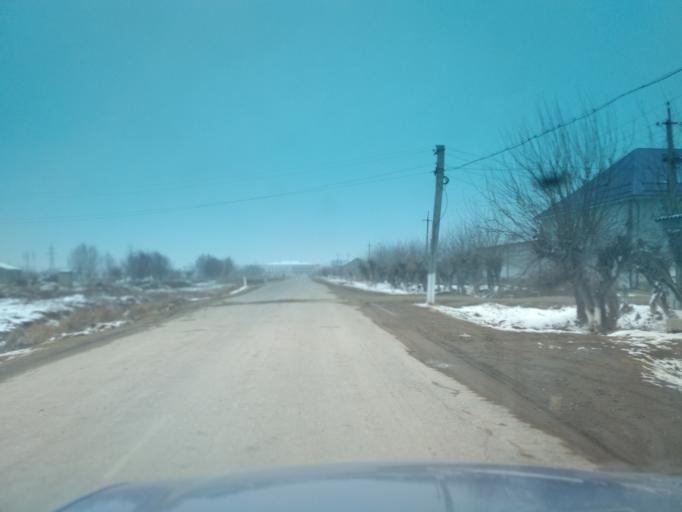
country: UZ
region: Sirdaryo
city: Guliston
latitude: 40.4828
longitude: 68.7515
